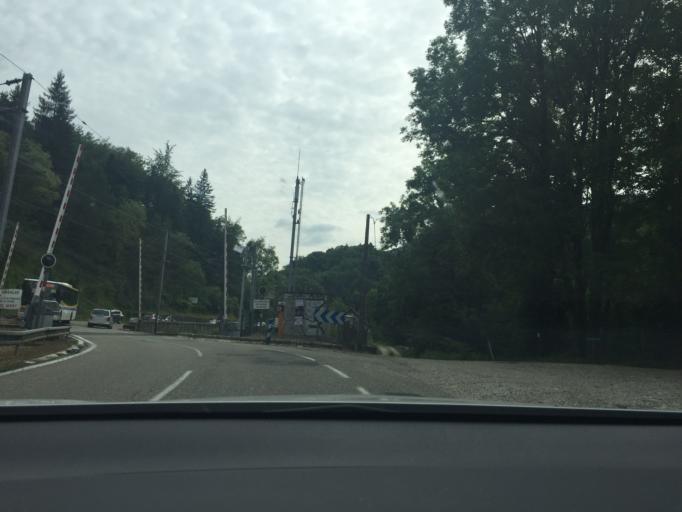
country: FR
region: Rhone-Alpes
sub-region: Departement de la Savoie
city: Vimines
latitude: 45.5338
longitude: 5.8648
